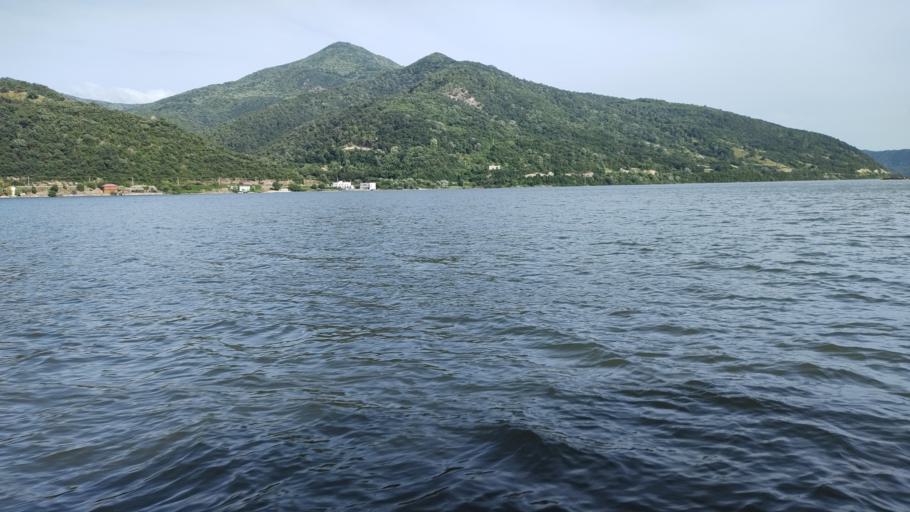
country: RO
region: Caras-Severin
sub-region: Comuna Berzasca
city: Berzasca
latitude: 44.5862
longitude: 22.0249
